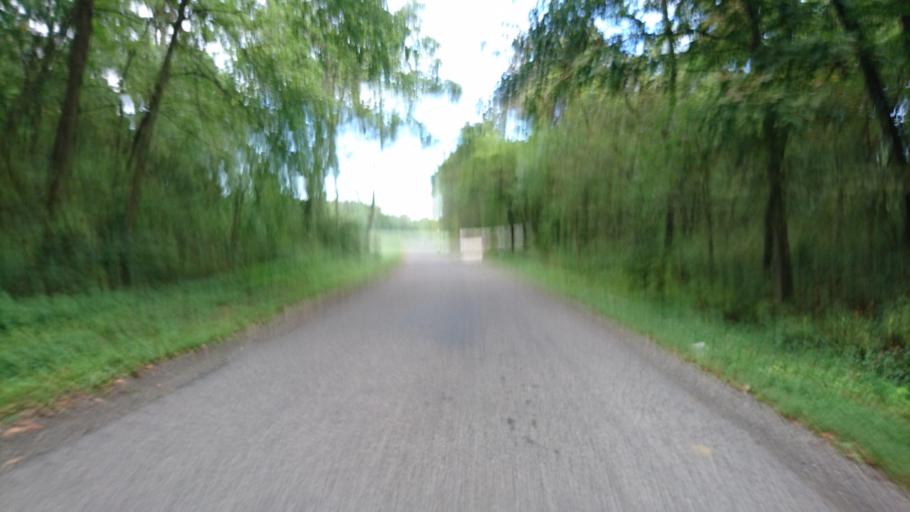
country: US
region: Illinois
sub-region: Macoupin County
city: Staunton
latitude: 38.9867
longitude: -89.7094
